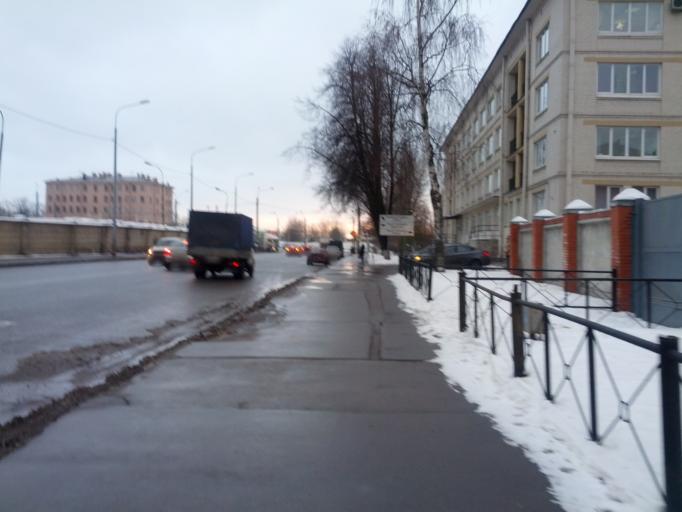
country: RU
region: St.-Petersburg
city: Centralniy
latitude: 59.9071
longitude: 30.3552
